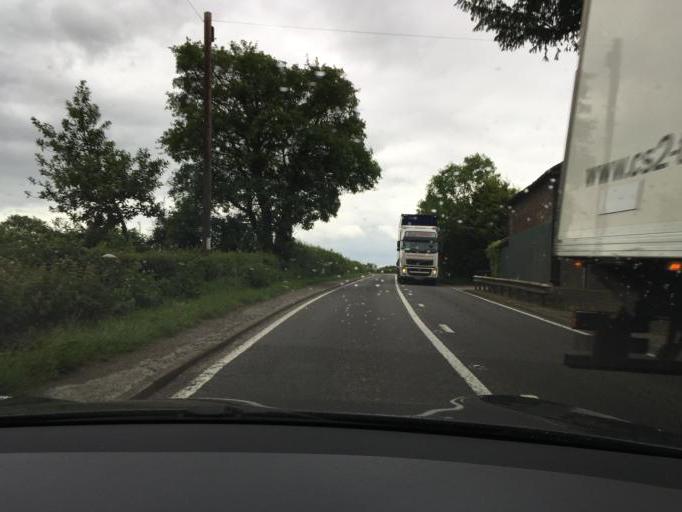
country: GB
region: England
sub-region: Derbyshire
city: Ashbourne
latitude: 53.0019
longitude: -1.7096
